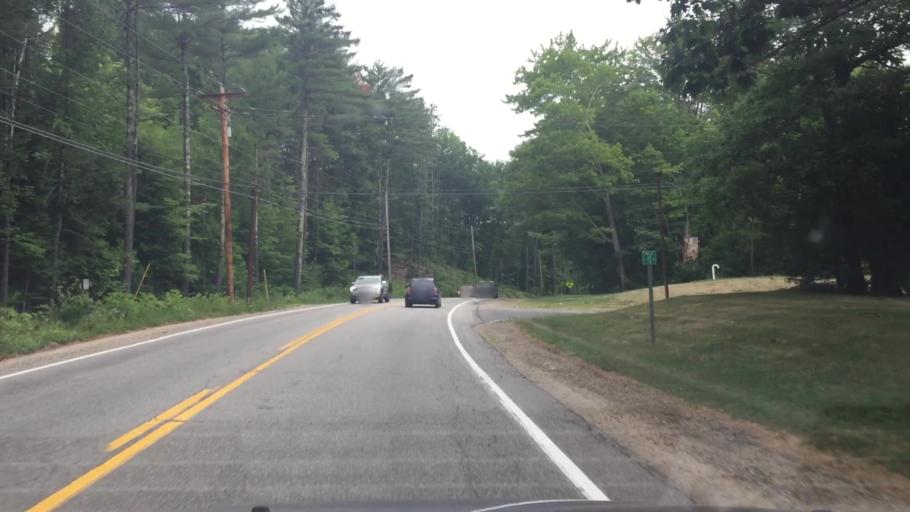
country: US
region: New Hampshire
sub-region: Carroll County
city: Moultonborough
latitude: 43.7412
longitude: -71.4130
